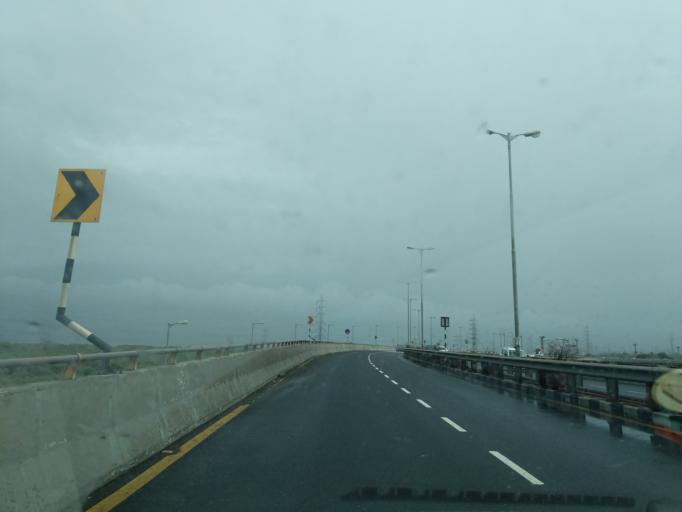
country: IN
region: Maharashtra
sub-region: Mumbai Suburban
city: Mumbai
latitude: 19.0138
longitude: 72.8717
